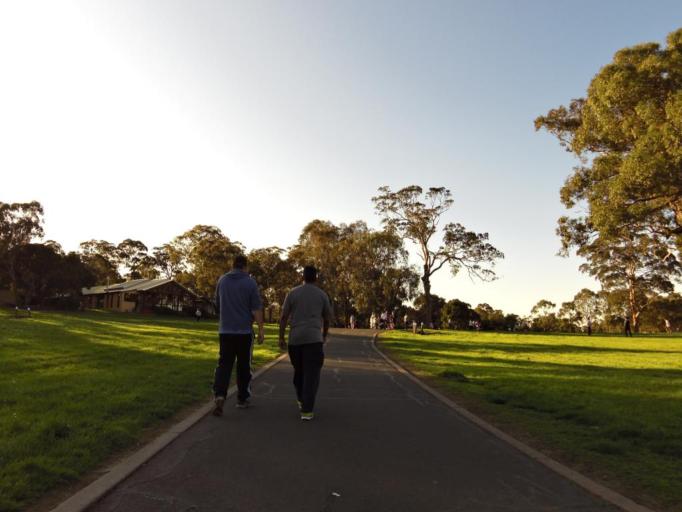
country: AU
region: Victoria
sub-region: Monash
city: Mulgrave
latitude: -37.8973
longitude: 145.1973
